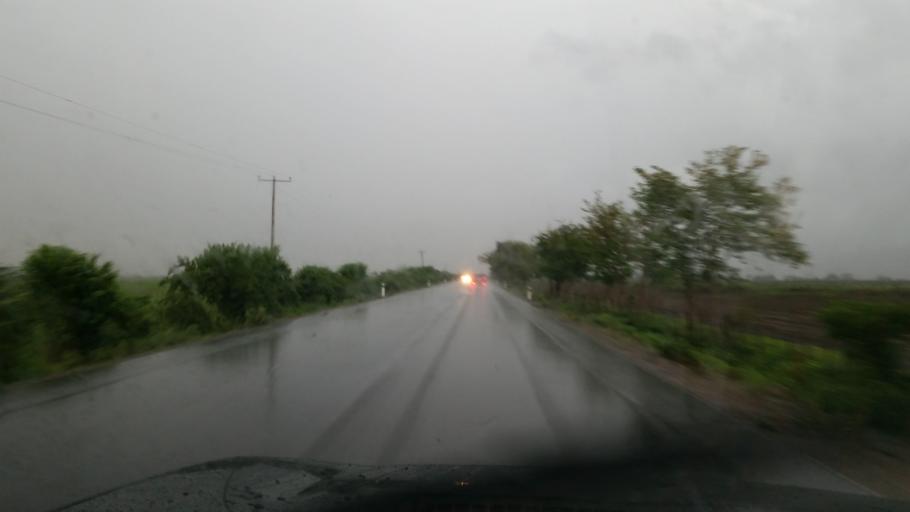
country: NI
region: Chinandega
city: Chichigalpa
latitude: 12.7819
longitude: -86.9337
